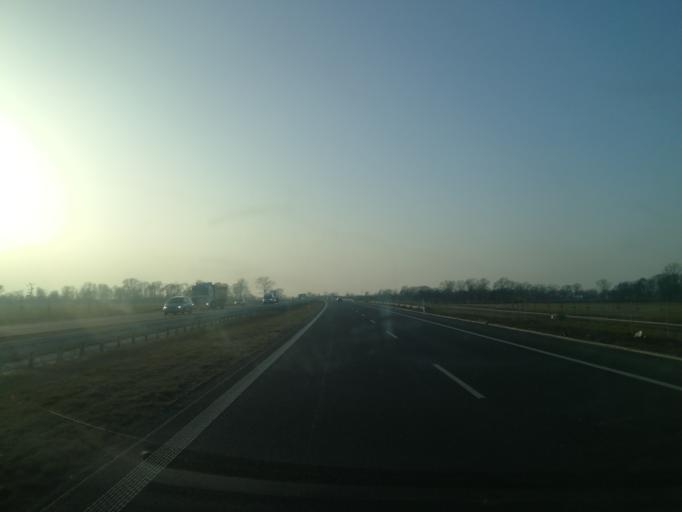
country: PL
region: Pomeranian Voivodeship
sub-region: Powiat nowodworski
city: Nowy Dwor Gdanski
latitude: 54.1728
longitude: 19.2092
